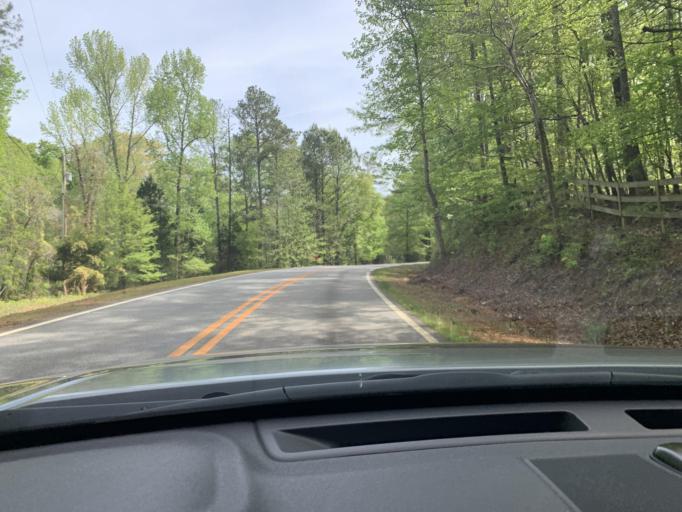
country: US
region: Georgia
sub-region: Oconee County
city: Watkinsville
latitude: 33.8441
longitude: -83.4740
